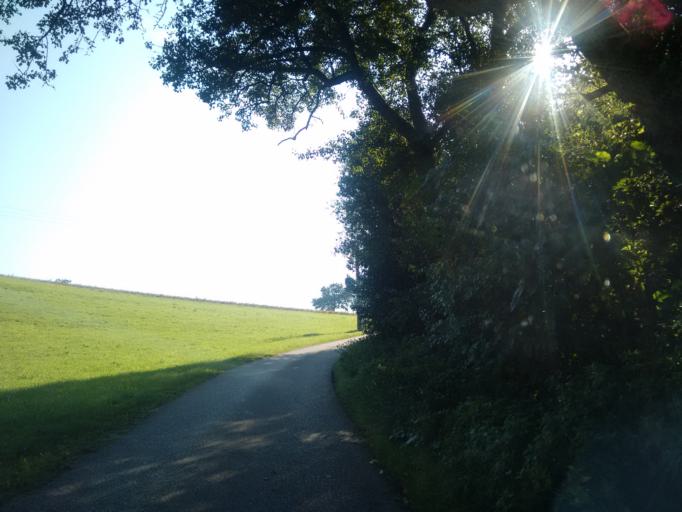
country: AT
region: Upper Austria
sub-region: Politischer Bezirk Linz-Land
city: Horsching
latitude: 48.1344
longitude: 14.2018
